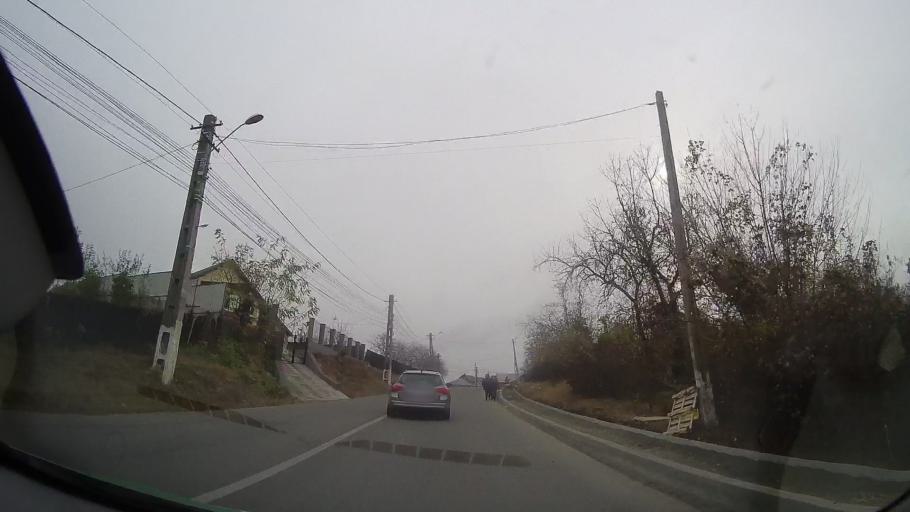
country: RO
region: Prahova
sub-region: Oras Baicoi
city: Tintea
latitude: 45.0325
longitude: 25.9039
